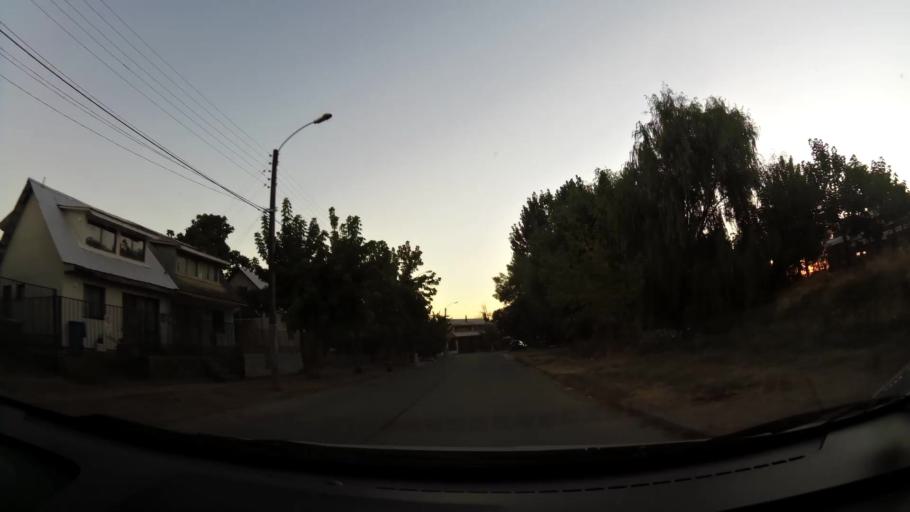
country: CL
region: Maule
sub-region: Provincia de Talca
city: Talca
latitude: -35.4492
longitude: -71.6278
